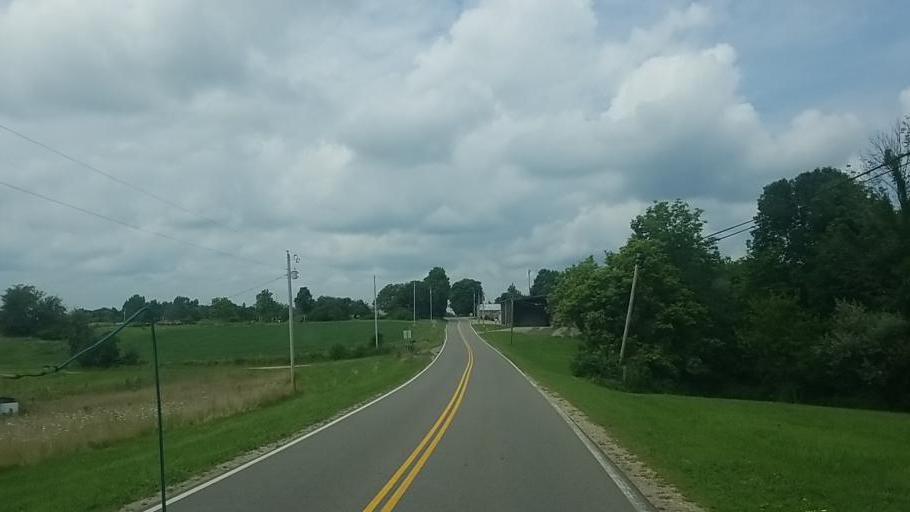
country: US
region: Ohio
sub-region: Licking County
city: Utica
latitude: 40.1985
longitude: -82.3376
